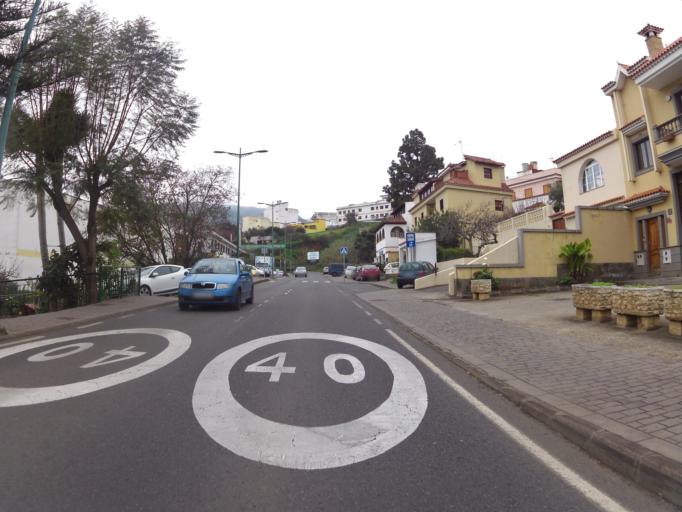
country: ES
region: Canary Islands
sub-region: Provincia de Las Palmas
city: Teror
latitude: 28.0631
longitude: -15.5392
